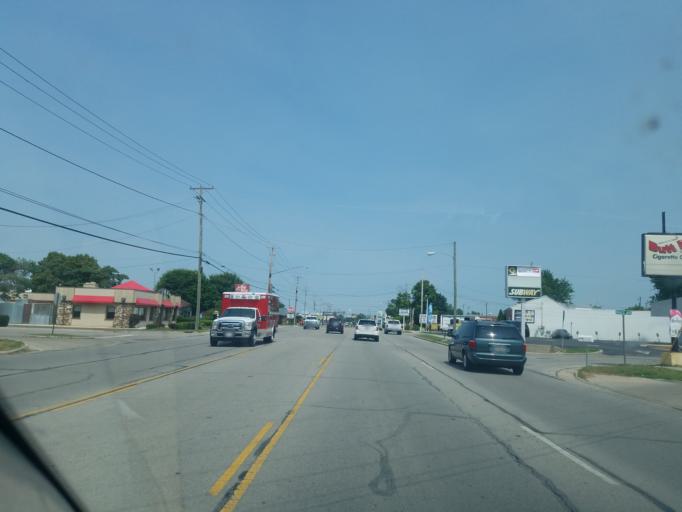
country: US
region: Ohio
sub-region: Seneca County
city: Tiffin
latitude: 41.1108
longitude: -83.2091
